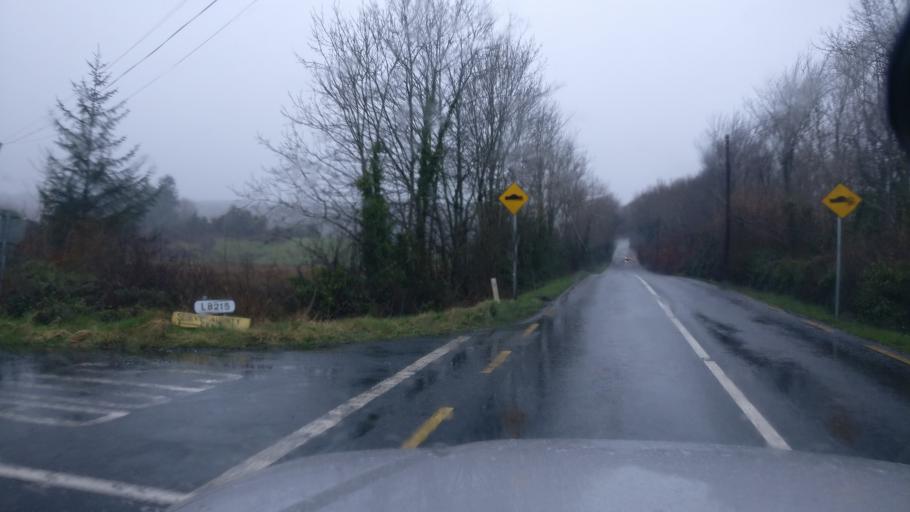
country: IE
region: Connaught
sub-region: County Galway
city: Loughrea
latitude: 53.1353
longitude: -8.4632
